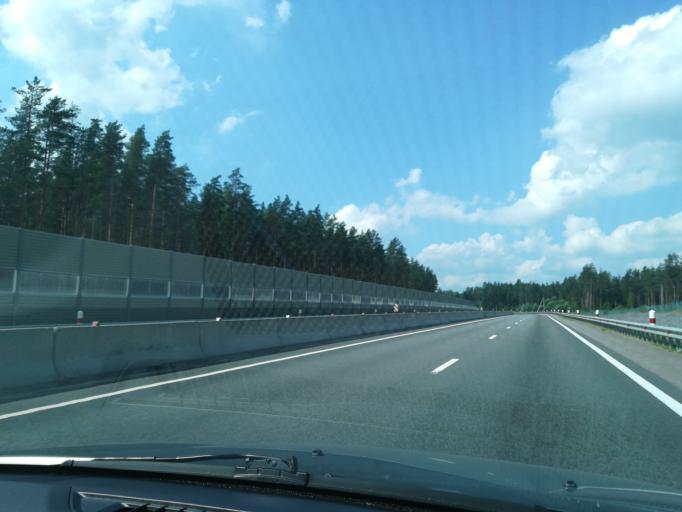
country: RU
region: Leningrad
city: Vistino
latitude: 59.6283
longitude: 28.6127
